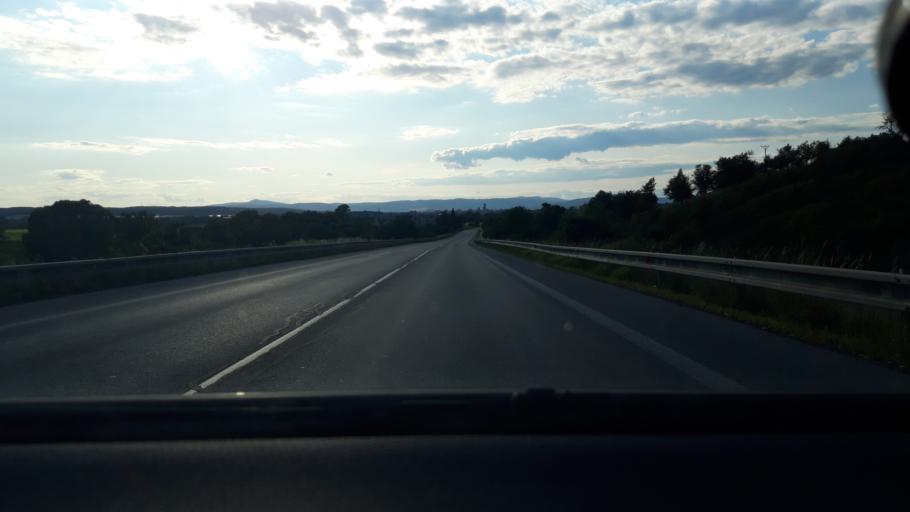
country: SK
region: Banskobystricky
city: Lucenec
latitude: 48.3087
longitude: 19.7142
